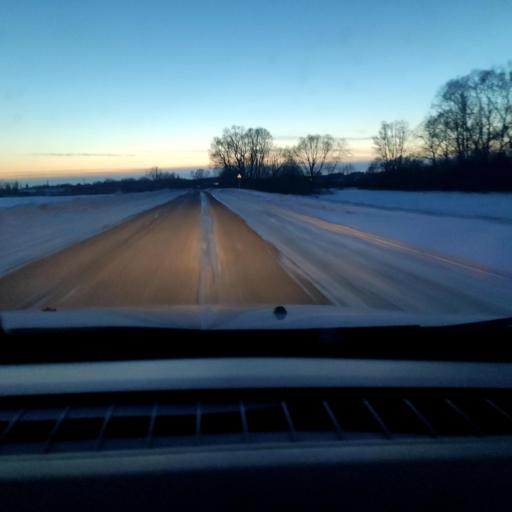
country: RU
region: Samara
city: Georgiyevka
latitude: 53.3325
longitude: 50.9113
